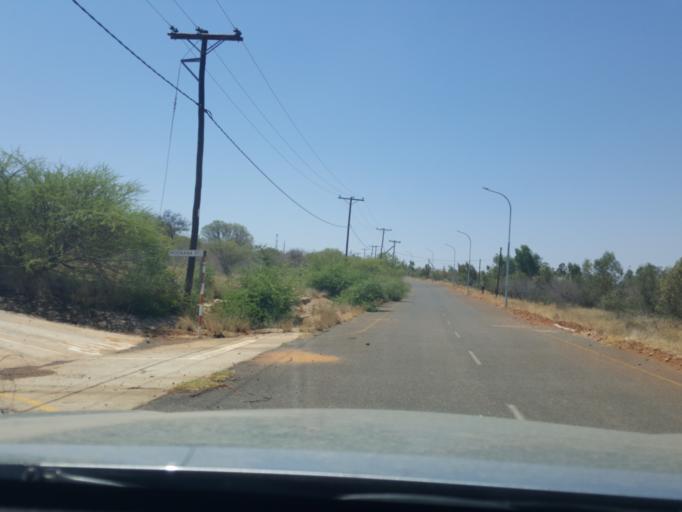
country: BW
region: South East
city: Lobatse
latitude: -25.1836
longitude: 25.6804
